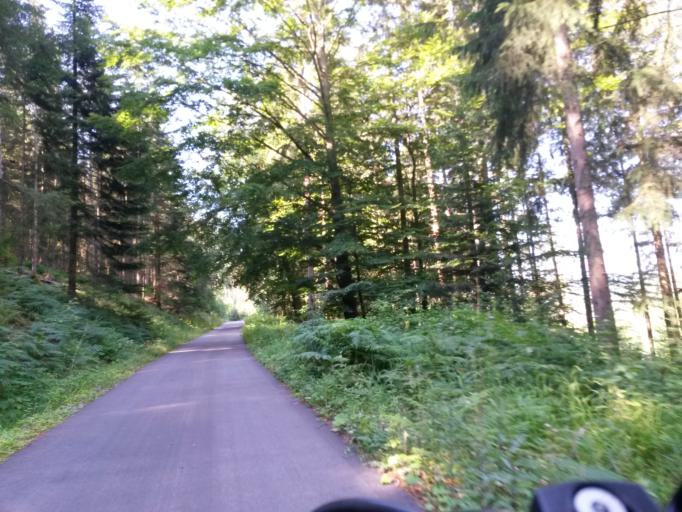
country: DE
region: Baden-Wuerttemberg
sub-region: Karlsruhe Region
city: Bad Wildbad
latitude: 48.7066
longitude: 8.5425
